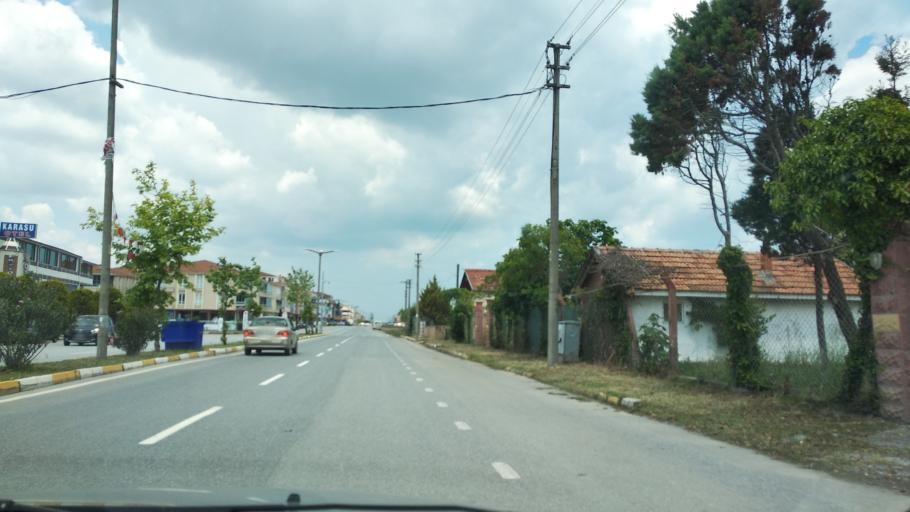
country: TR
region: Sakarya
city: Karasu
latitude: 41.1130
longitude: 30.6846
